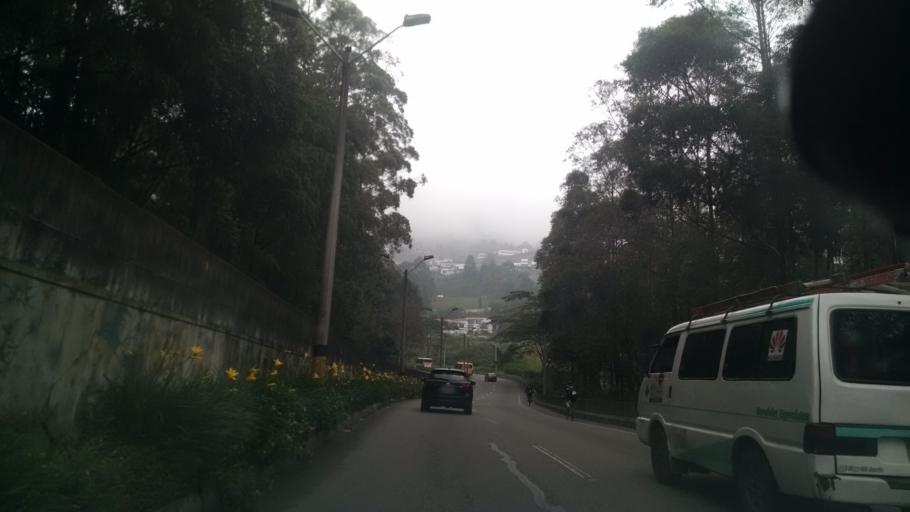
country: CO
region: Antioquia
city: Medellin
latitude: 6.2136
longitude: -75.5502
